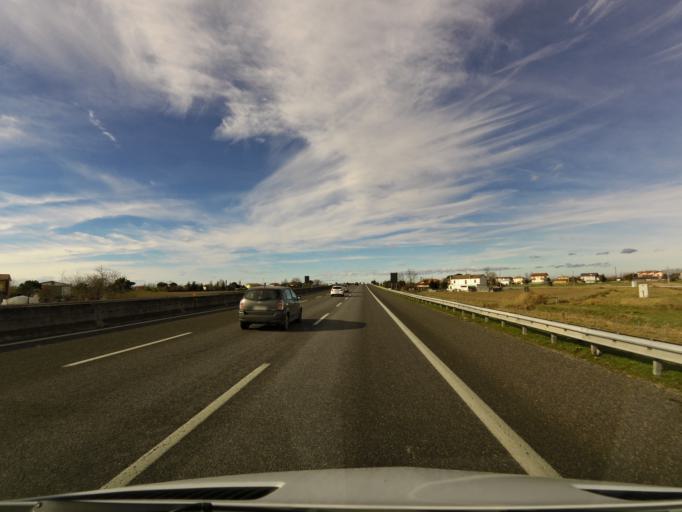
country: IT
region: Emilia-Romagna
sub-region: Forli-Cesena
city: Gatteo-Sant'Angelo
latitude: 44.1265
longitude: 12.3811
